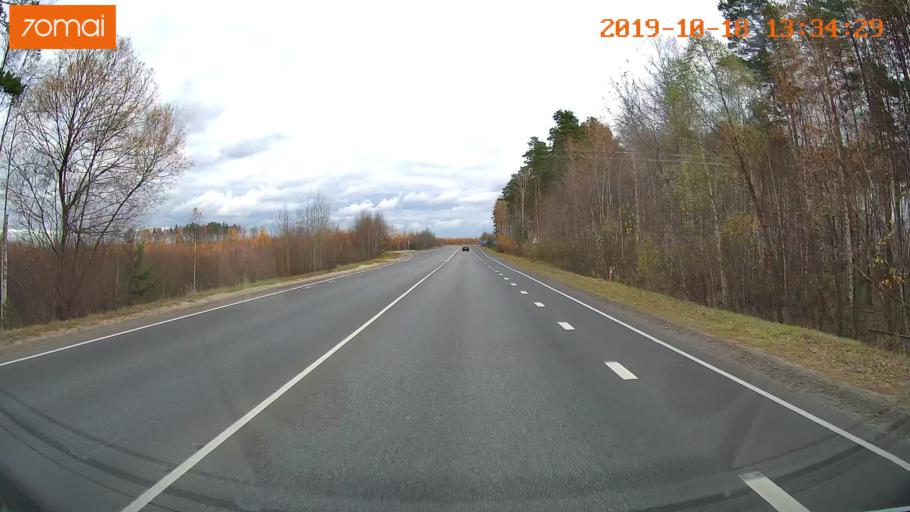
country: RU
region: Rjazan
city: Solotcha
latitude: 54.8545
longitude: 39.9555
